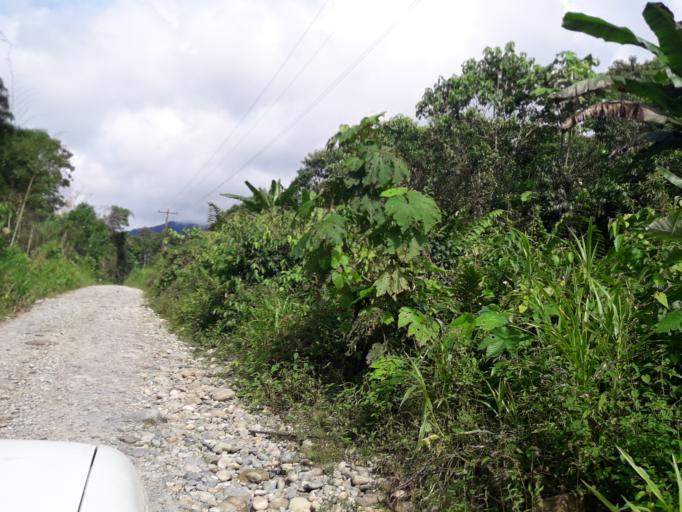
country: EC
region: Napo
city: Archidona
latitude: -0.9420
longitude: -77.8822
